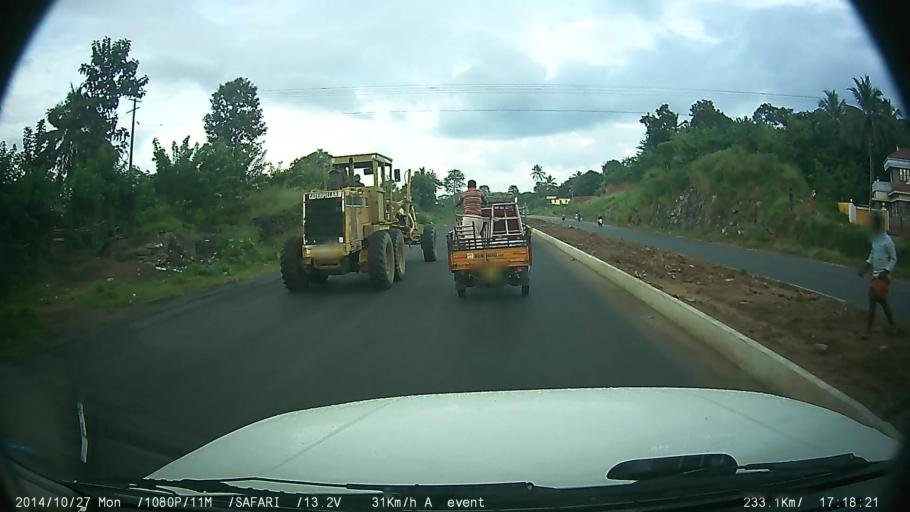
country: IN
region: Kerala
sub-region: Thrissur District
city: Chelakara
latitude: 10.6352
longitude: 76.5191
